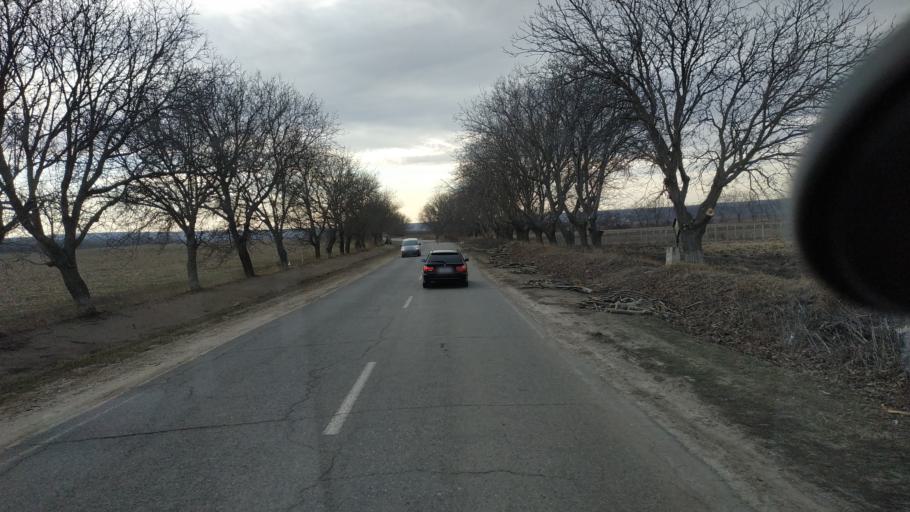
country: MD
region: Criuleni
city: Criuleni
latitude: 47.1585
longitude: 29.1112
